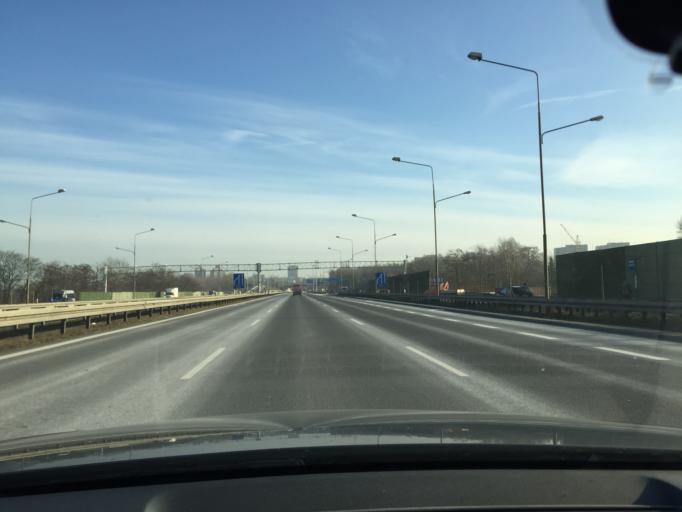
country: PL
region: Silesian Voivodeship
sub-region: Katowice
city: Katowice
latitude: 50.2520
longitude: 18.9891
